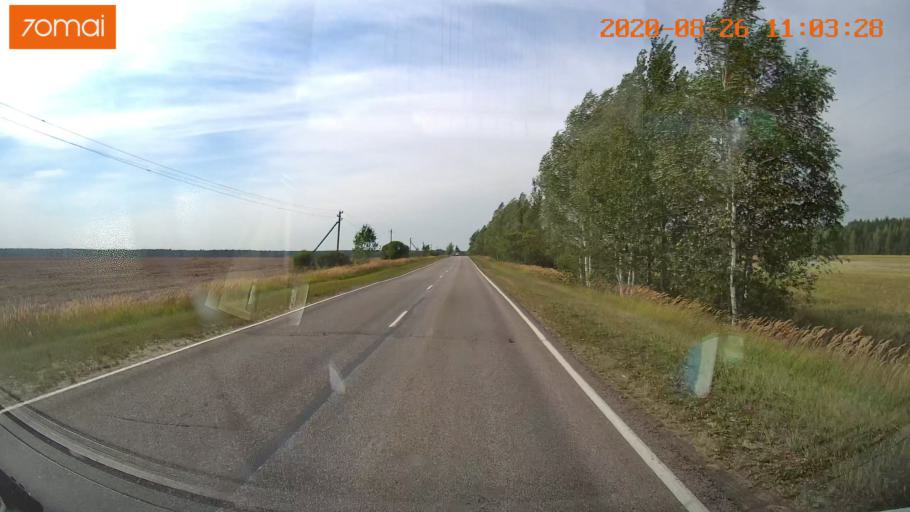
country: RU
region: Rjazan
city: Izhevskoye
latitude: 54.5404
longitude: 41.2110
